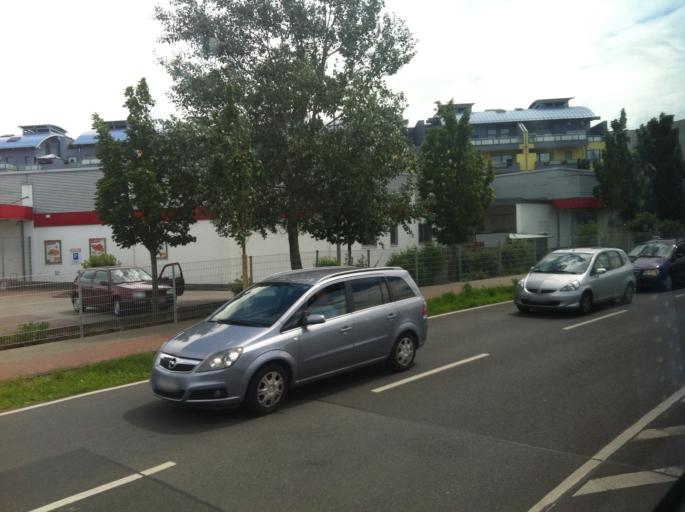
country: DE
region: Rheinland-Pfalz
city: Budenheim
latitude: 50.0100
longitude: 8.2163
